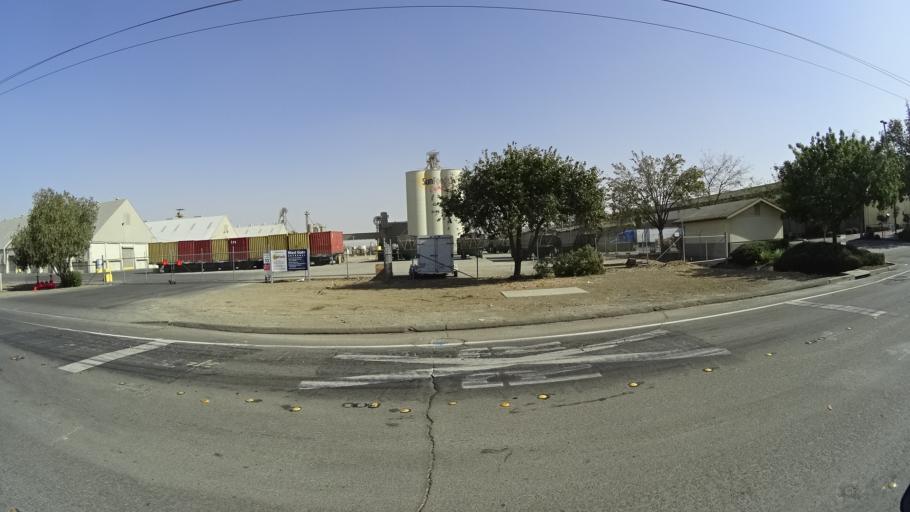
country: US
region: California
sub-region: Yolo County
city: Woodland
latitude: 38.6901
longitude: -121.7469
